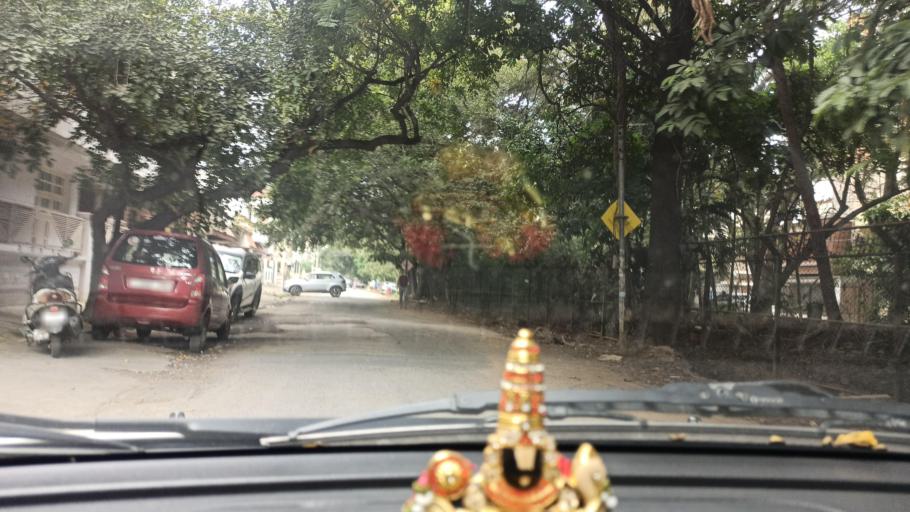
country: IN
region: Karnataka
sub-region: Bangalore Urban
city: Bangalore
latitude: 13.0187
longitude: 77.6448
